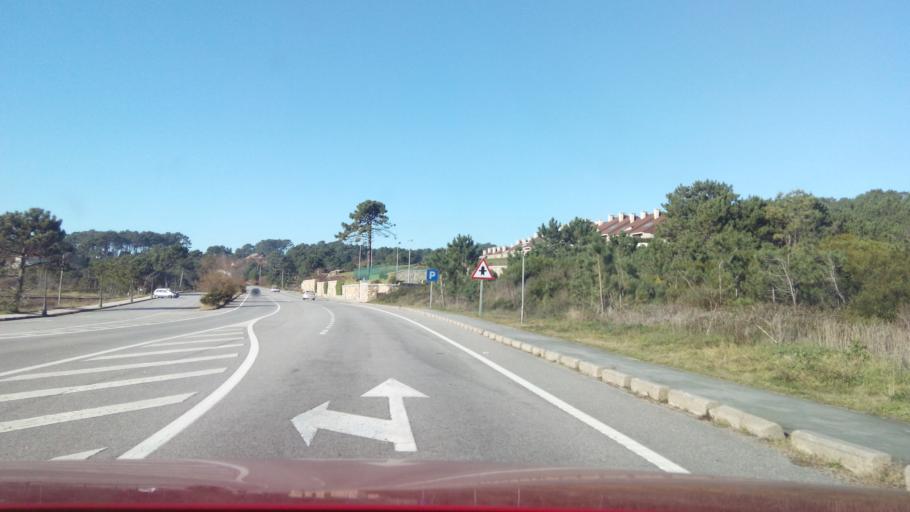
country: ES
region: Galicia
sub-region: Provincia de Pontevedra
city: O Grove
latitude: 42.4614
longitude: -8.8962
